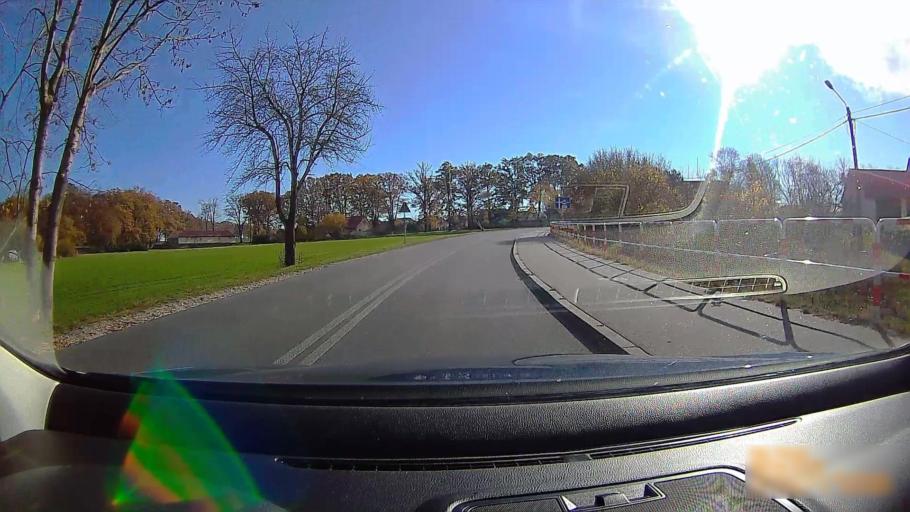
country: PL
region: Greater Poland Voivodeship
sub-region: Powiat ostrzeszowski
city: Doruchow
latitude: 51.3606
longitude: 18.0295
